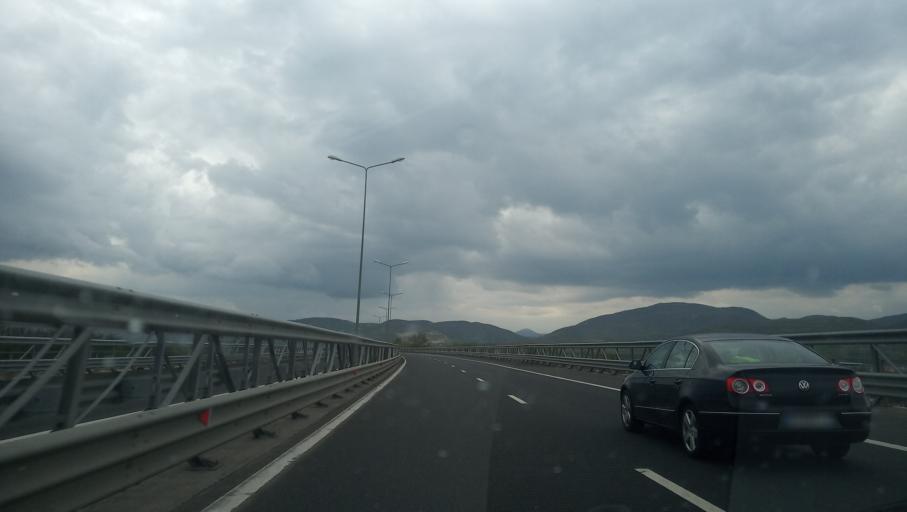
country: RO
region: Hunedoara
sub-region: Oras Simeria
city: Simeria
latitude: 45.8628
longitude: 23.0264
